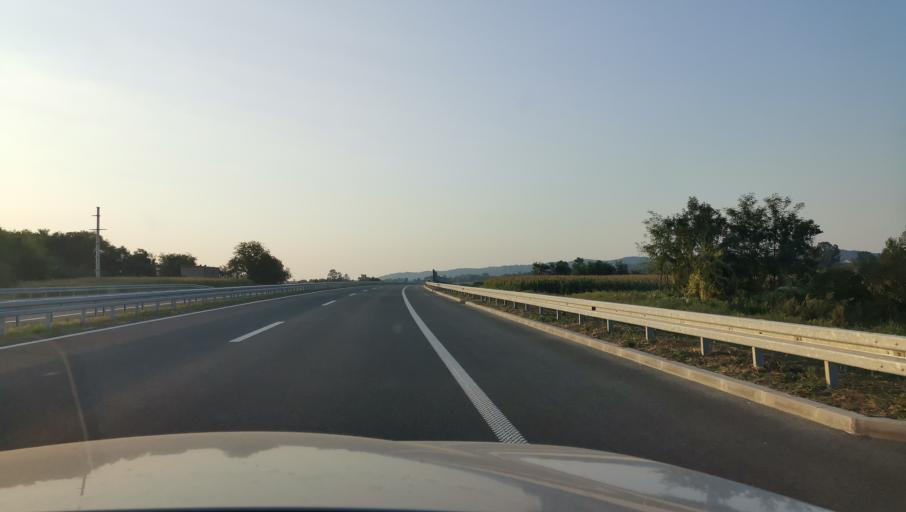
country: RS
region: Central Serbia
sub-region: Kolubarski Okrug
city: Ljig
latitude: 44.2953
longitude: 20.2360
